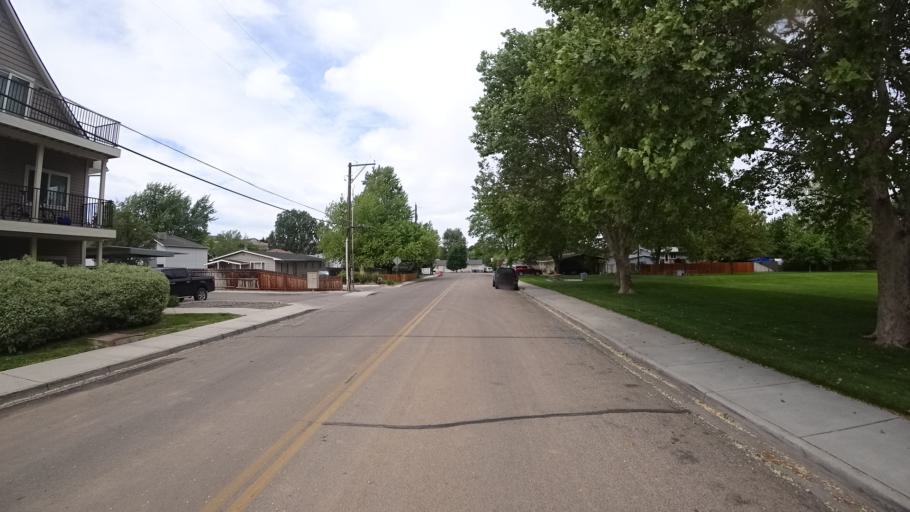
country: US
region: Idaho
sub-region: Ada County
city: Boise
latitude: 43.5772
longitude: -116.2174
